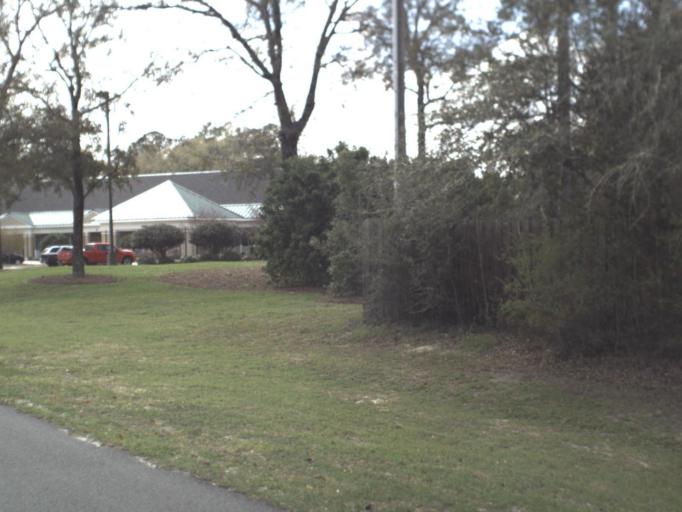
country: US
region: Florida
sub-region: Wakulla County
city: Crawfordville
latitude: 30.2043
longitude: -84.3673
